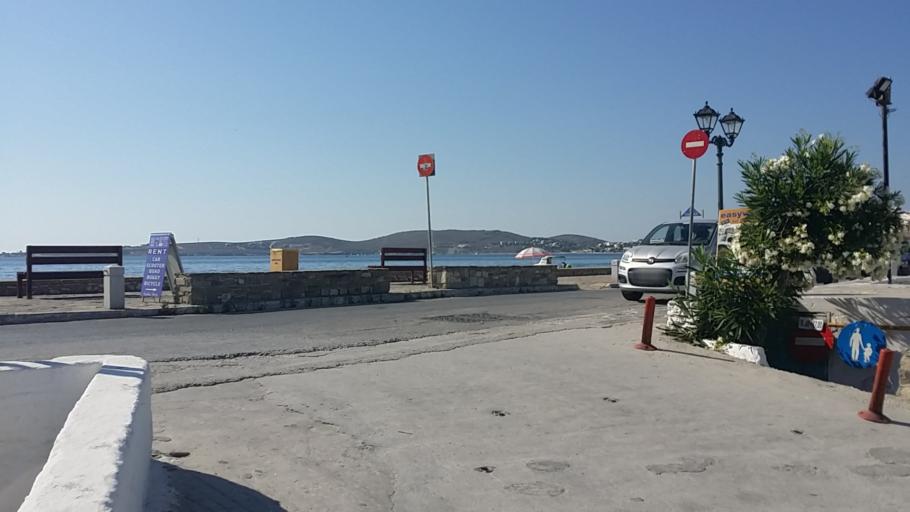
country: GR
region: South Aegean
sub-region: Nomos Kykladon
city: Paros
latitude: 37.0819
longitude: 25.1461
